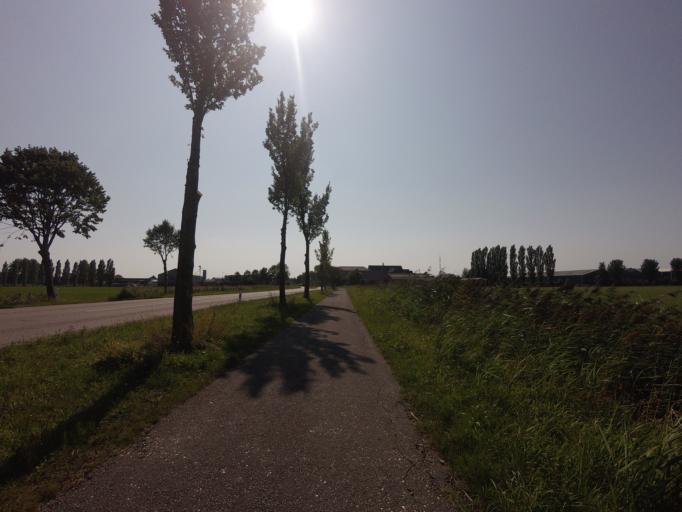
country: NL
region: Groningen
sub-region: Gemeente Zuidhorn
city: Grijpskerk
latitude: 53.2693
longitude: 6.3076
